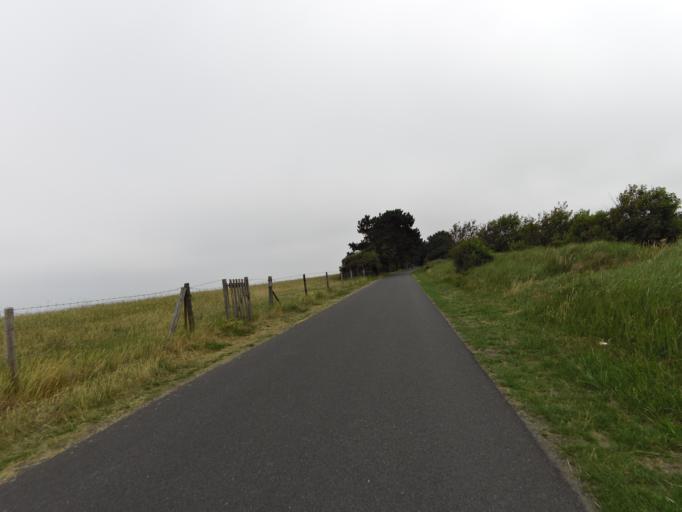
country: DE
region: Lower Saxony
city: Cuxhaven
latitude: 53.8753
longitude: 8.6140
